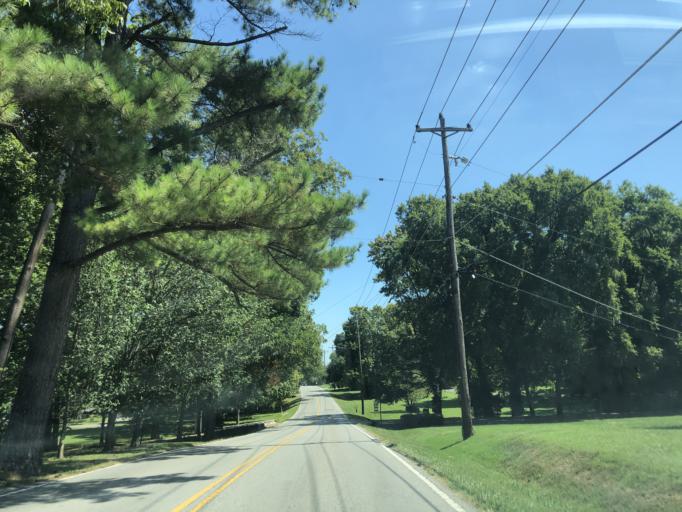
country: US
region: Tennessee
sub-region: Davidson County
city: Oak Hill
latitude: 36.0805
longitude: -86.7966
